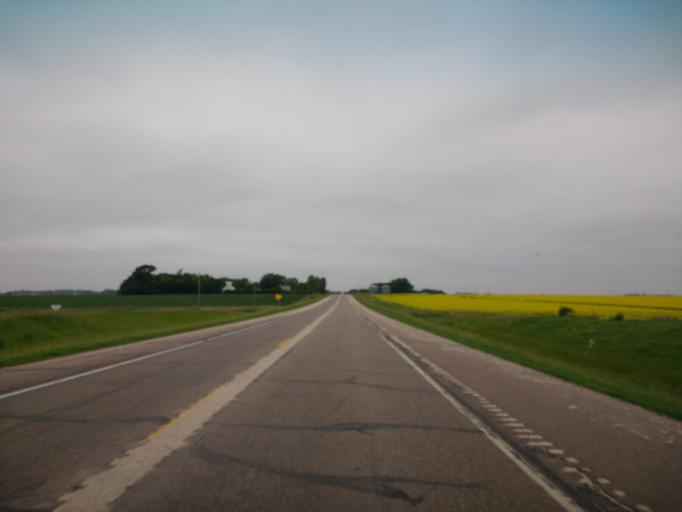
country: US
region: Iowa
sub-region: O'Brien County
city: Hartley
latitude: 43.1846
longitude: -95.4403
